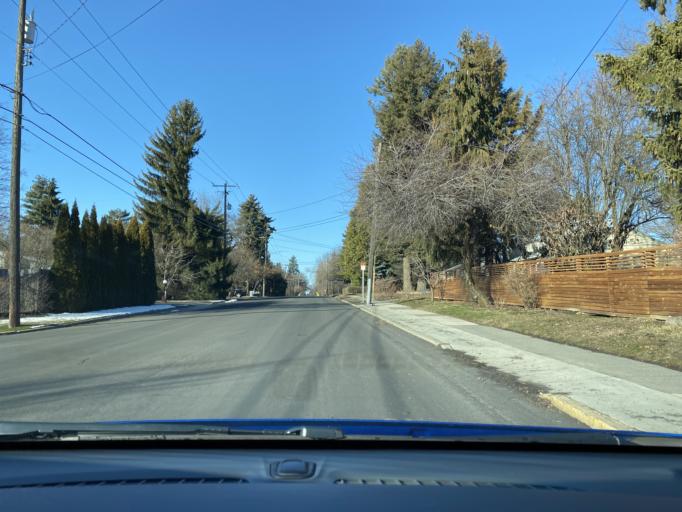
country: US
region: Idaho
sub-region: Latah County
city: Moscow
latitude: 46.7375
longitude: -116.9857
